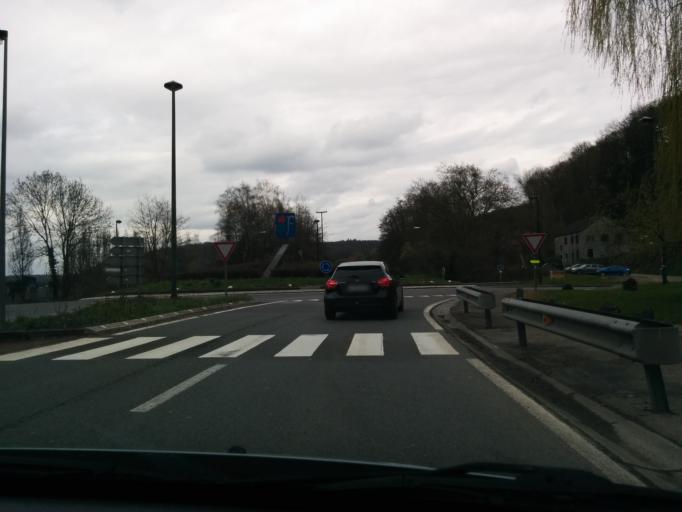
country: BE
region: Wallonia
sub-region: Province de Namur
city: Floreffe
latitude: 50.4297
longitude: 4.7583
